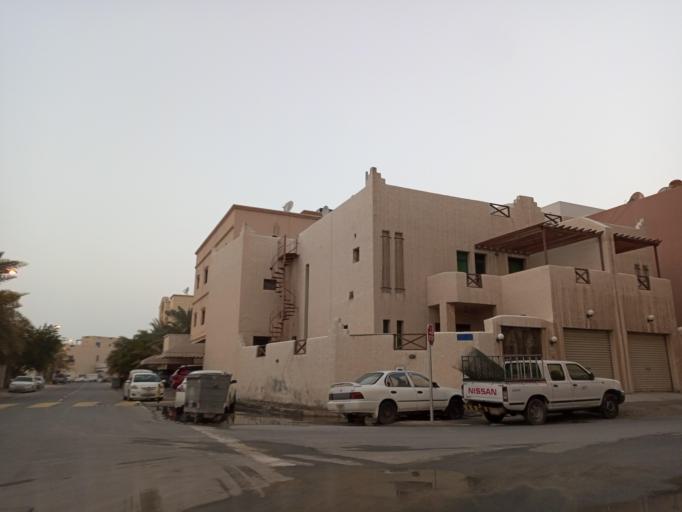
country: BH
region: Muharraq
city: Al Hadd
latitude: 26.2305
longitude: 50.6553
